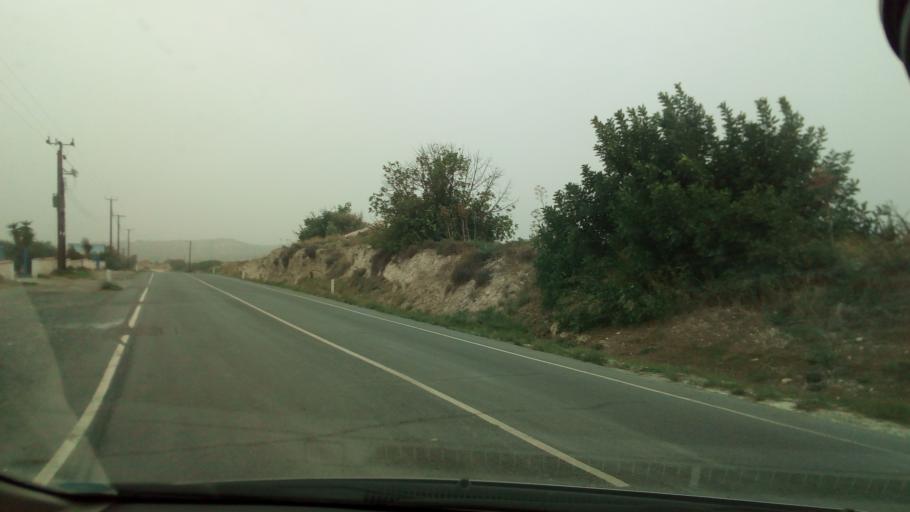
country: CY
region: Larnaka
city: Kofinou
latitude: 34.7757
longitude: 33.3332
